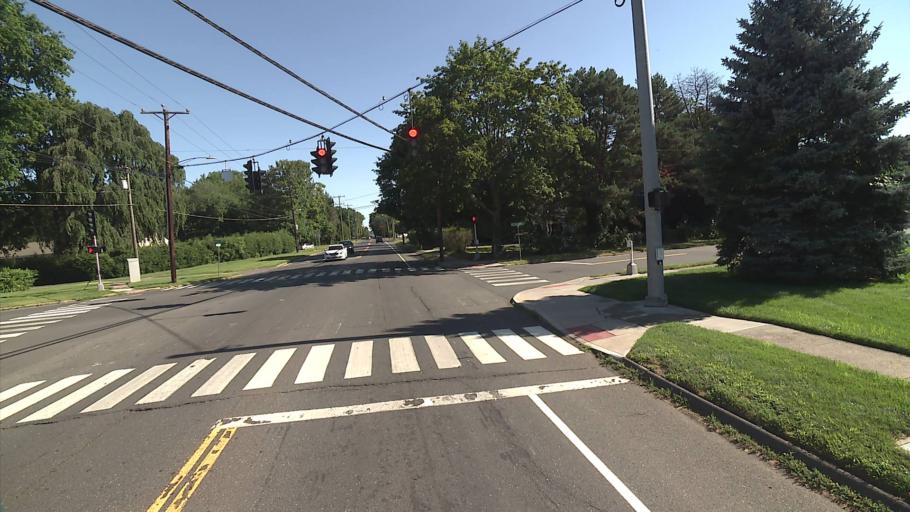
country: US
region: Connecticut
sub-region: New Haven County
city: Cheshire Village
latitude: 41.5152
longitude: -72.8983
